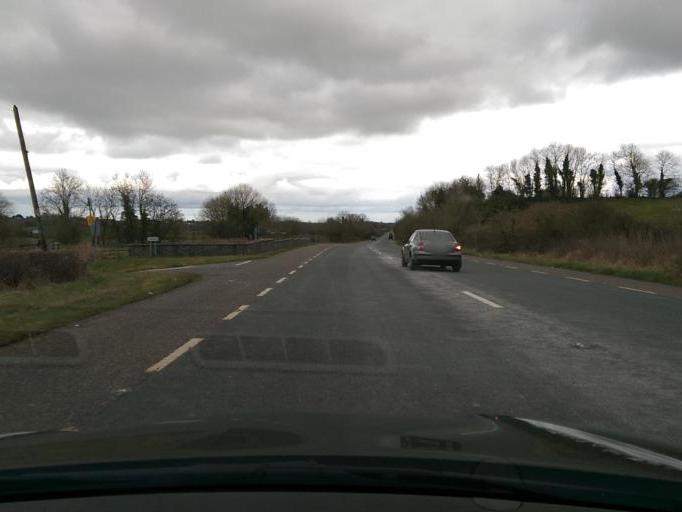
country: IE
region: Leinster
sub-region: Uibh Fhaili
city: Clara
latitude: 53.3976
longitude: -7.6480
